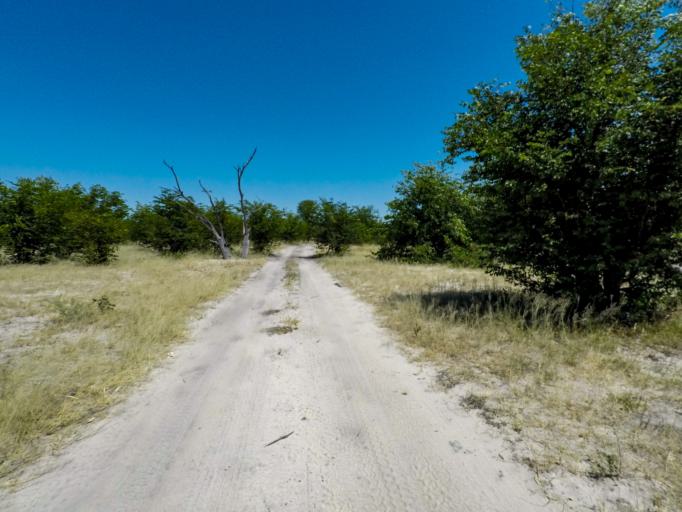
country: BW
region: North West
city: Maun
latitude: -19.4346
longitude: 23.5675
